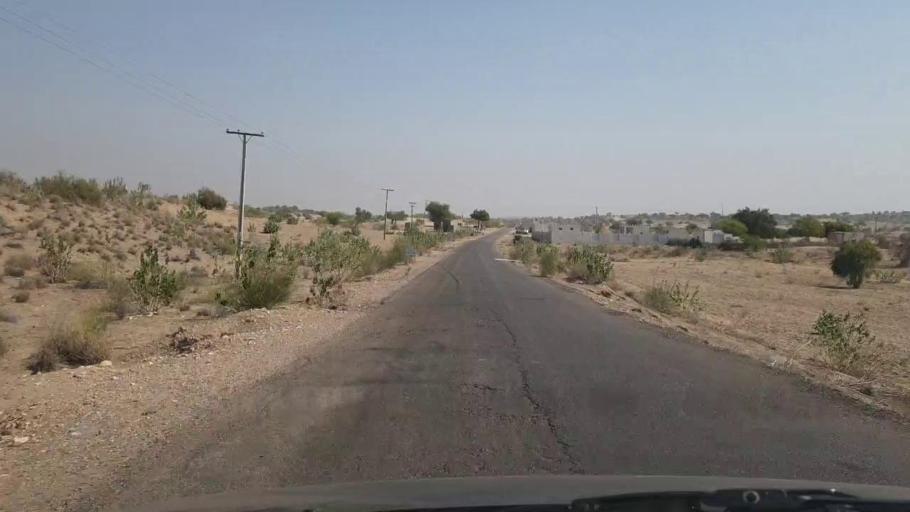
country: PK
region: Sindh
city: Chor
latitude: 25.5905
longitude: 69.9461
